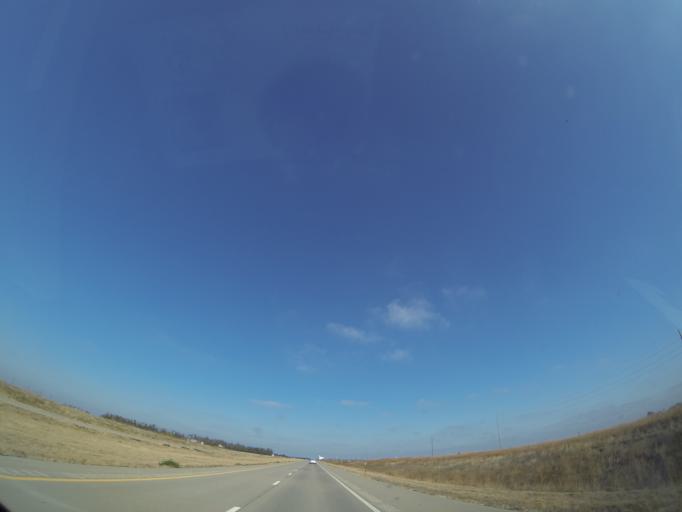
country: US
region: Kansas
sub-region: McPherson County
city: Inman
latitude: 38.2062
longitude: -97.7976
